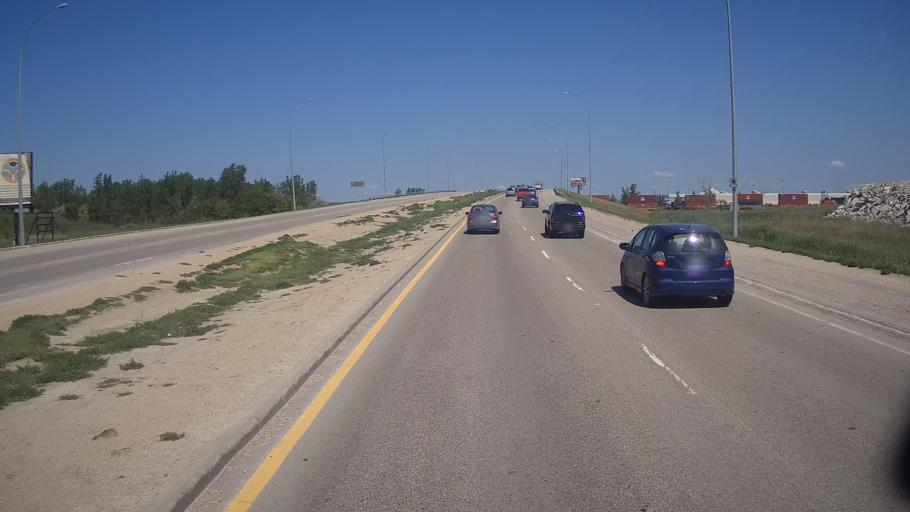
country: CA
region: Manitoba
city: Winnipeg
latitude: 49.8913
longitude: -97.0718
